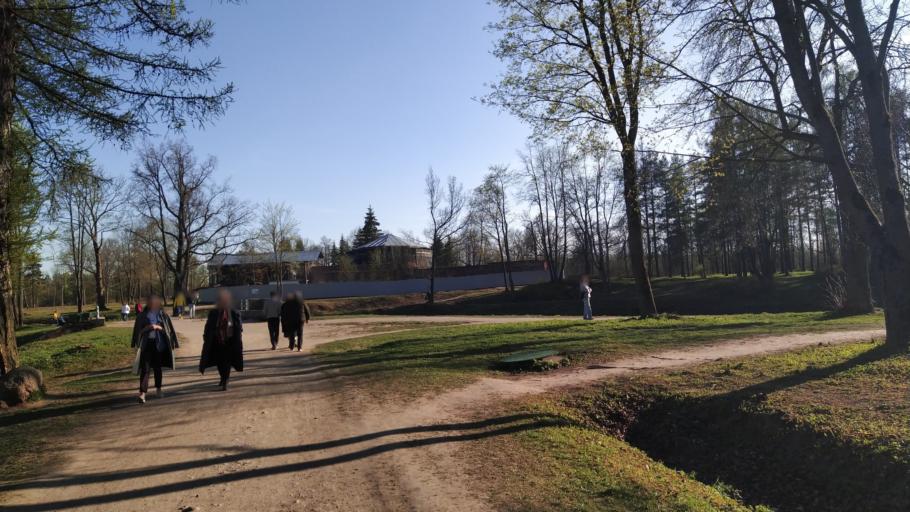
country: RU
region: St.-Petersburg
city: Aleksandrovskaya
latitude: 59.7097
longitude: 30.3453
